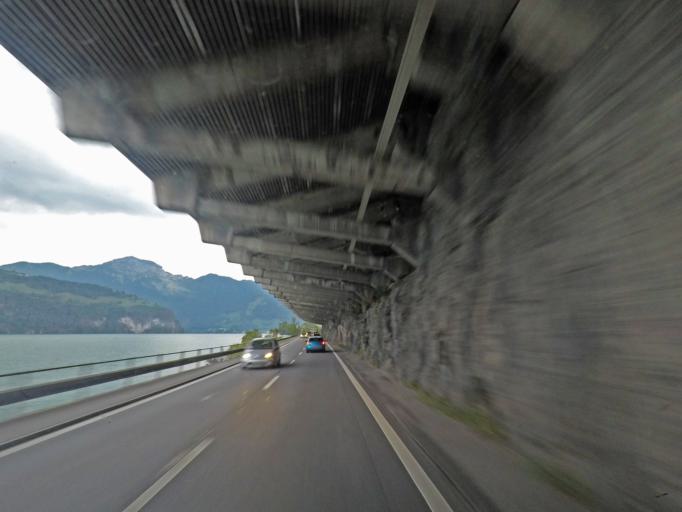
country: CH
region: Schwyz
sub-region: Bezirk Schwyz
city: Ingenbohl
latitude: 46.9643
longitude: 8.6158
